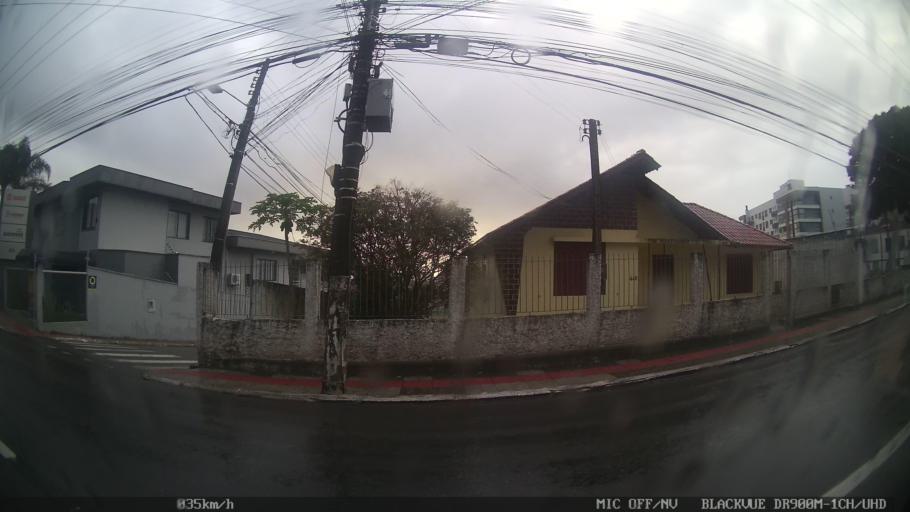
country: BR
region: Santa Catarina
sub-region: Sao Jose
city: Campinas
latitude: -27.6115
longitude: -48.6275
